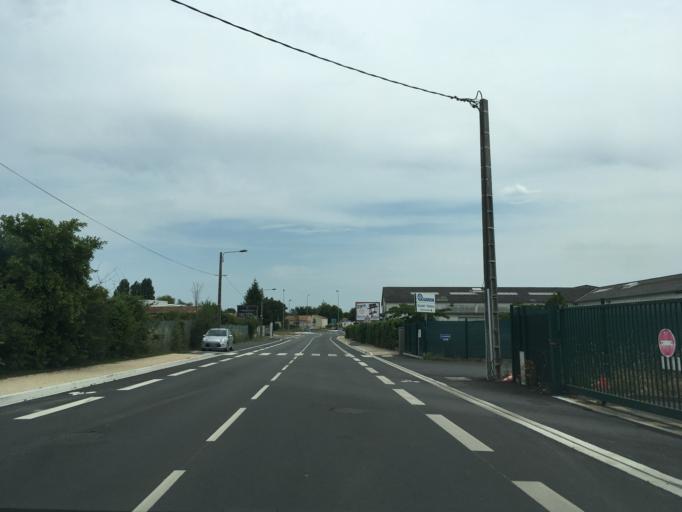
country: FR
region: Poitou-Charentes
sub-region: Departement des Deux-Sevres
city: Bessines
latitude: 46.3148
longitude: -0.5010
